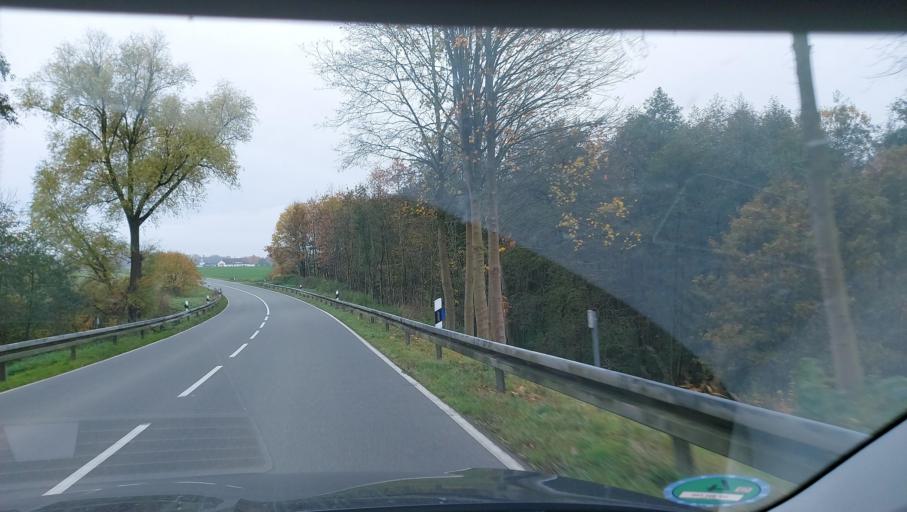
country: DE
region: Lower Saxony
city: Neuenkirchen
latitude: 52.1291
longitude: 8.3916
